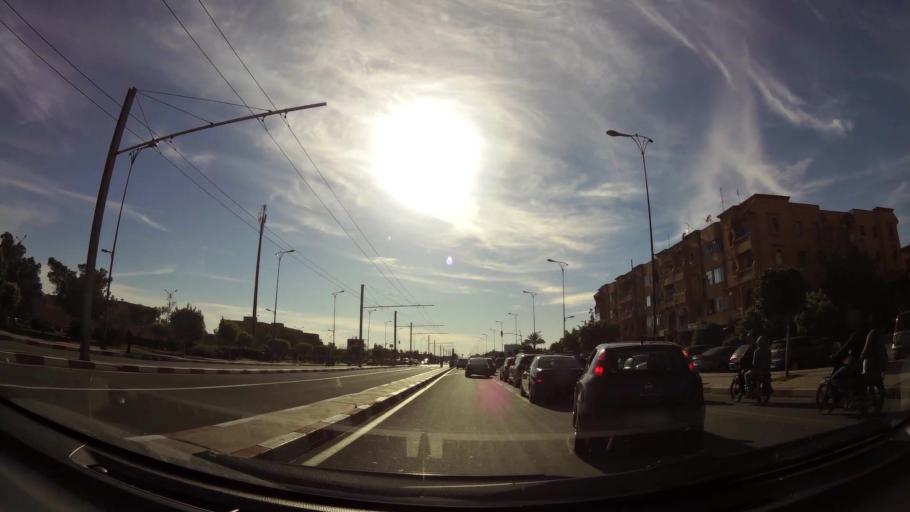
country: MA
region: Marrakech-Tensift-Al Haouz
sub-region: Marrakech
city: Marrakesh
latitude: 31.6278
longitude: -8.0453
